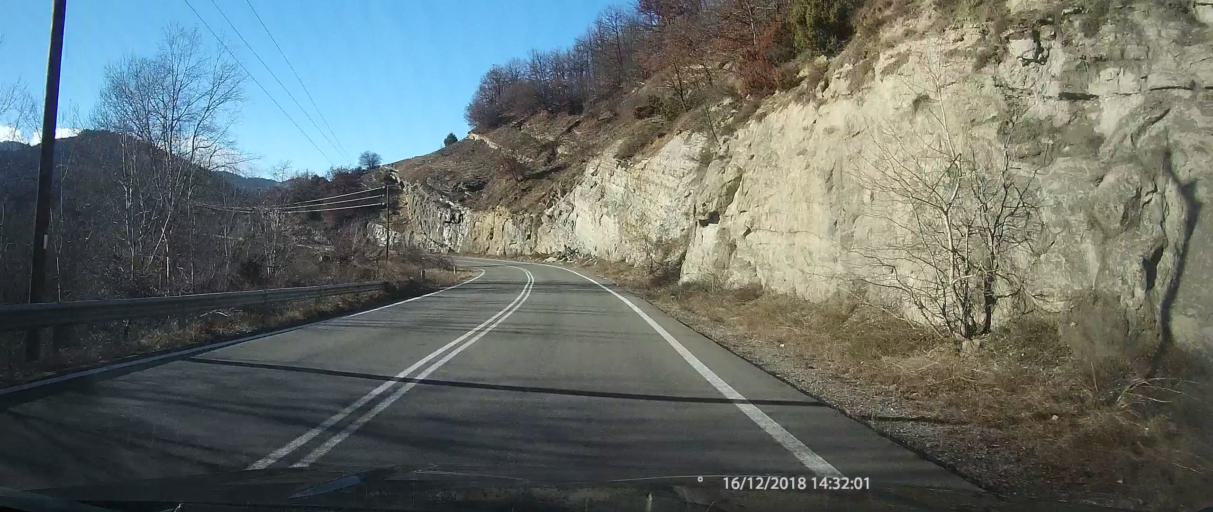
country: GR
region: West Macedonia
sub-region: Nomos Kozanis
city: Tsotili
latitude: 40.1950
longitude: 21.1752
